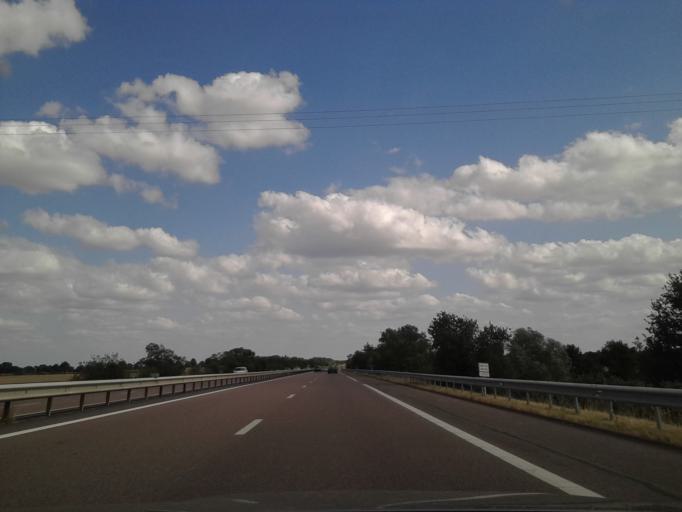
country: FR
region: Auvergne
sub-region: Departement de l'Allier
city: Estivareilles
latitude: 46.4783
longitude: 2.6709
